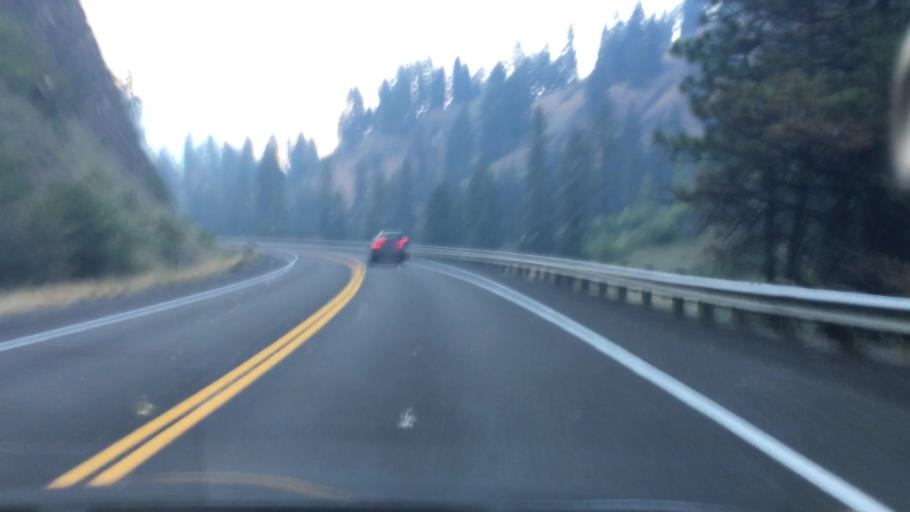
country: US
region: Idaho
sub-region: Valley County
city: McCall
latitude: 45.2348
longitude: -116.3258
